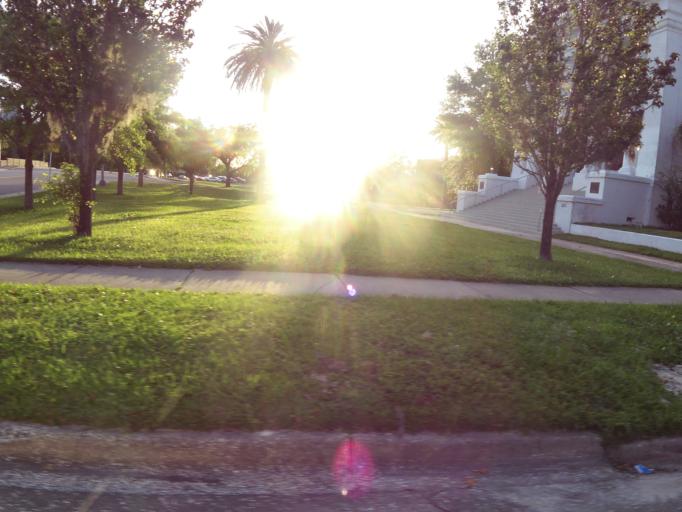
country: US
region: Florida
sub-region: Duval County
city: Jacksonville
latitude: 30.3368
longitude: -81.6566
